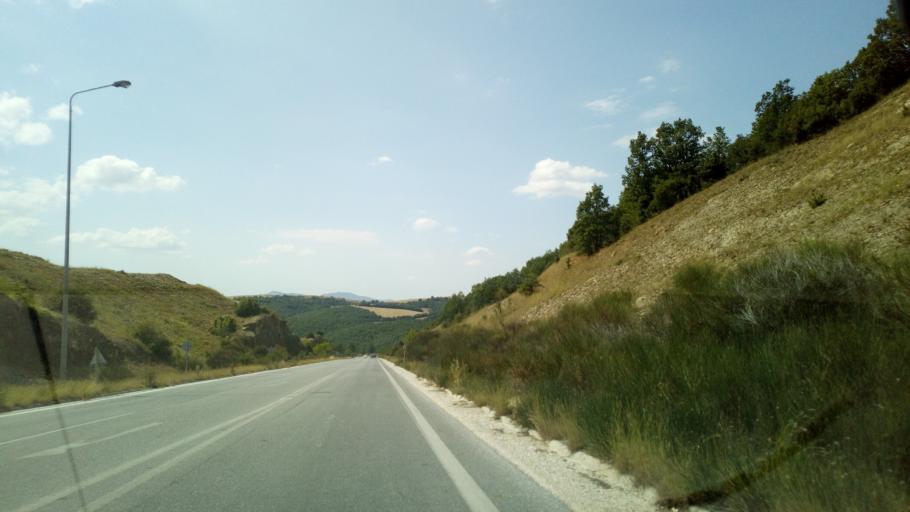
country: GR
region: Central Macedonia
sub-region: Nomos Chalkidikis
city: Polygyros
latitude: 40.4429
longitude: 23.4216
